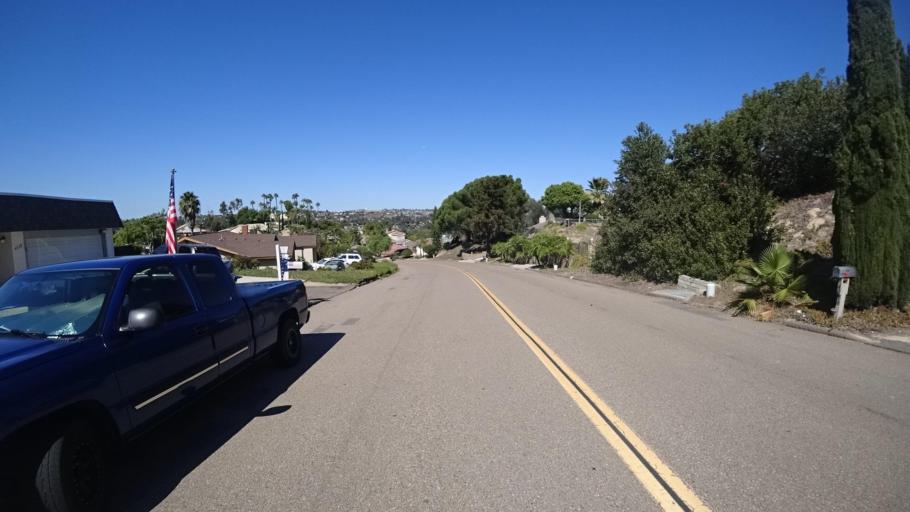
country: US
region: California
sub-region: San Diego County
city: Bonita
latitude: 32.6619
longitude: -117.0190
